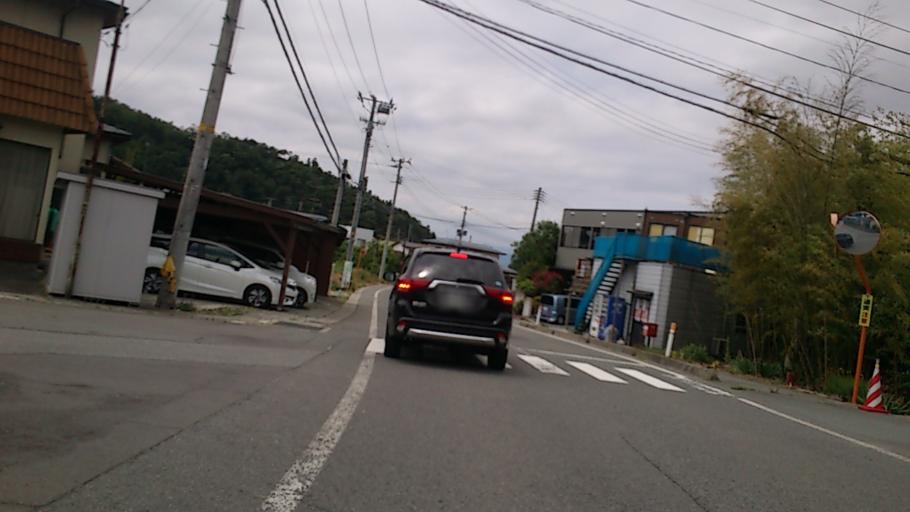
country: JP
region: Yamagata
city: Tendo
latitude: 38.3152
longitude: 140.3965
